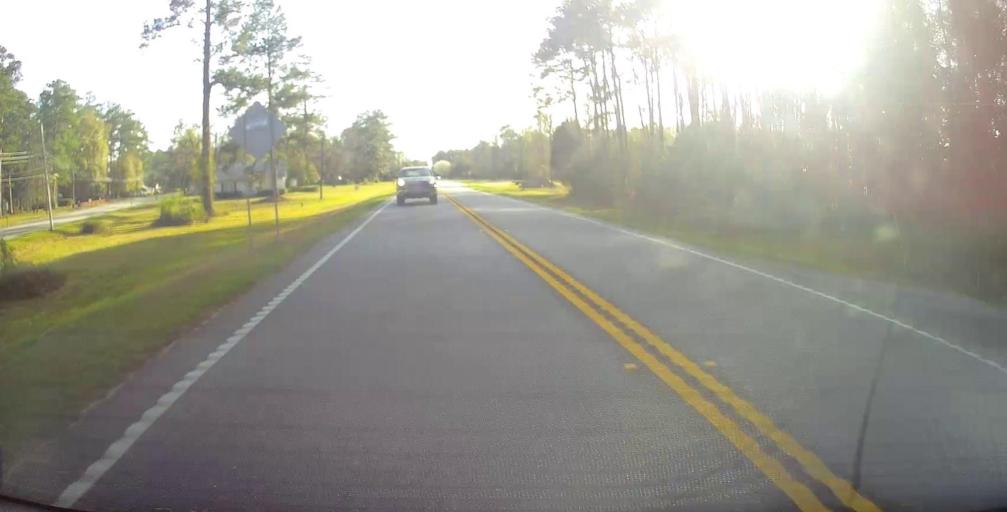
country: US
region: Georgia
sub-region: Tattnall County
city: Reidsville
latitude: 32.0941
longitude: -82.1105
